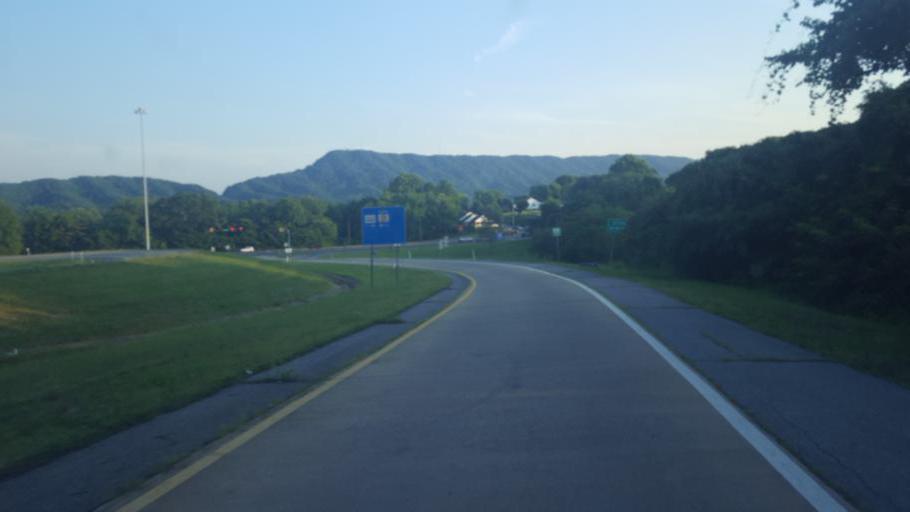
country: US
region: Tennessee
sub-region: Sullivan County
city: Kingsport
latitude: 36.5580
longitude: -82.5844
